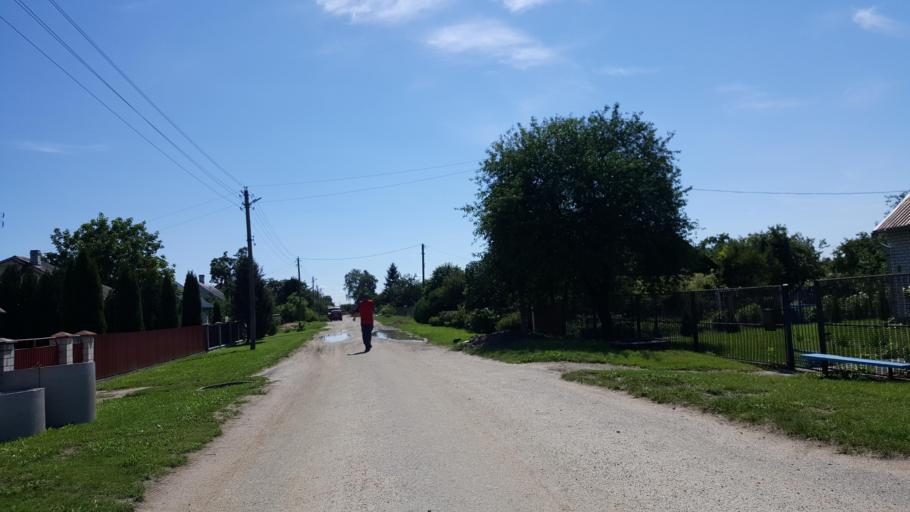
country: BY
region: Brest
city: Charnawchytsy
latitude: 52.2265
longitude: 23.7316
